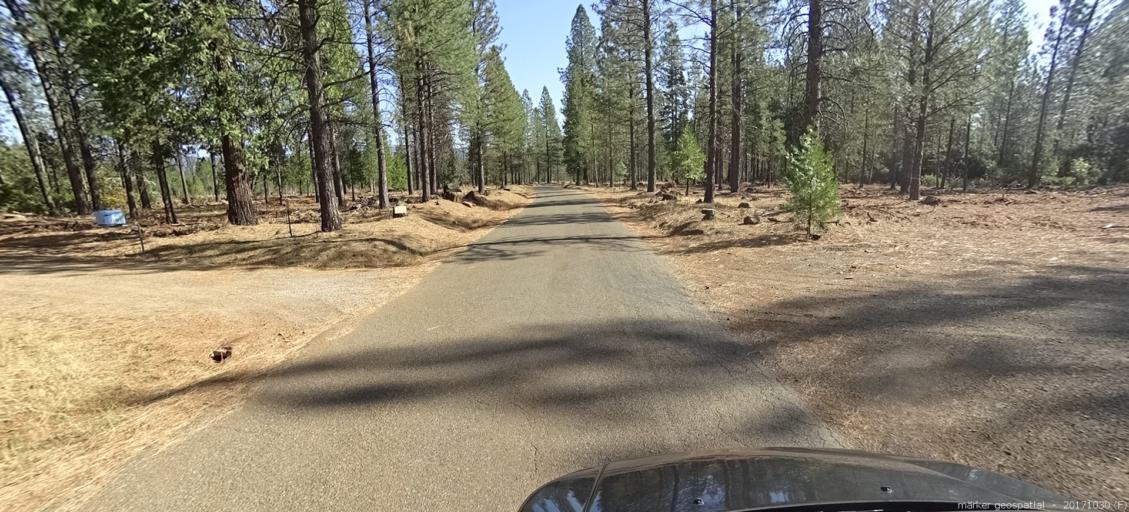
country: US
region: California
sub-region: Shasta County
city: Shingletown
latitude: 40.6102
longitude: -121.8674
